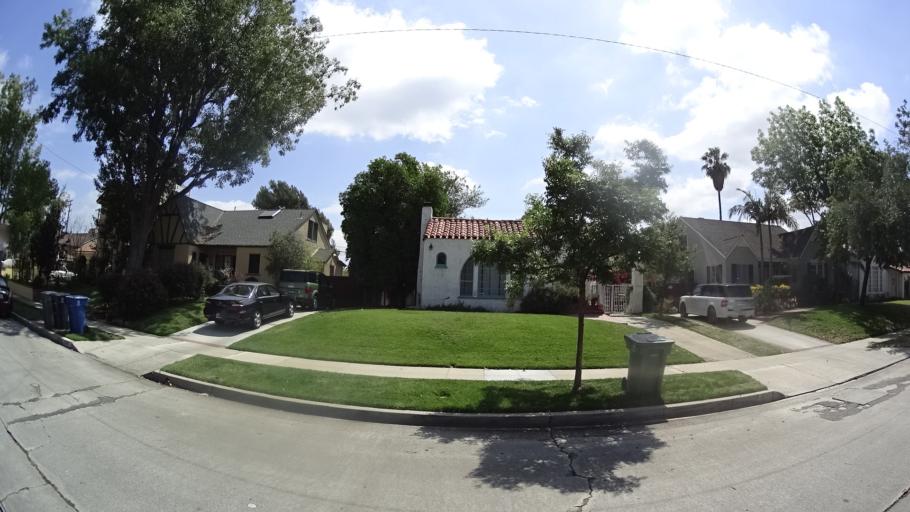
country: US
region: California
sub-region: Los Angeles County
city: North Hollywood
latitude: 34.1638
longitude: -118.3561
